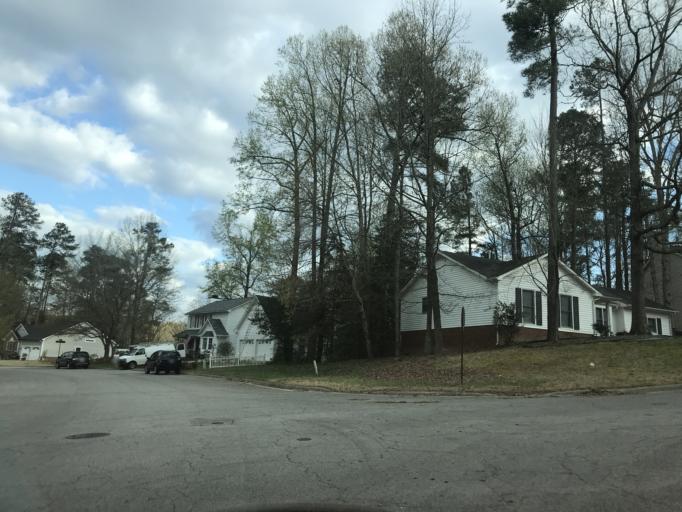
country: US
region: North Carolina
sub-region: Wake County
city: Knightdale
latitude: 35.8656
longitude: -78.5623
